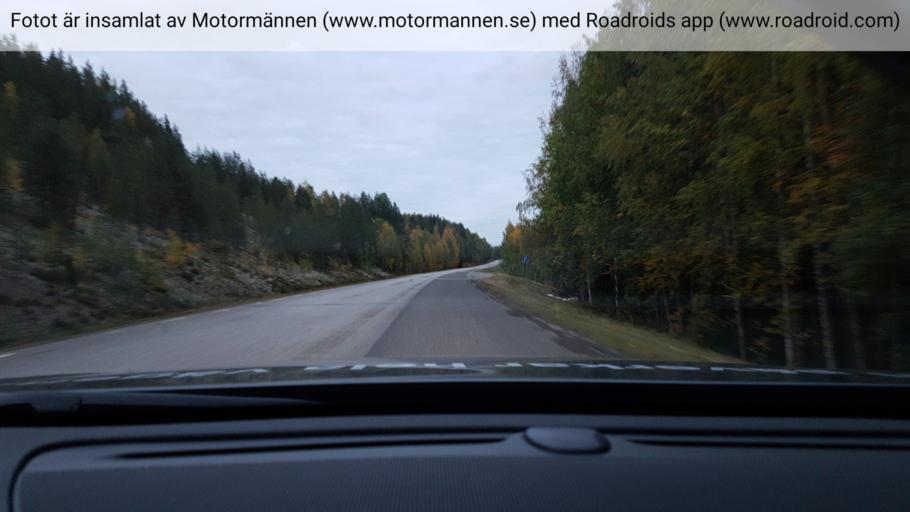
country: SE
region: Norrbotten
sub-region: Alvsbyns Kommun
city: AElvsbyn
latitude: 65.8520
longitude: 20.4474
